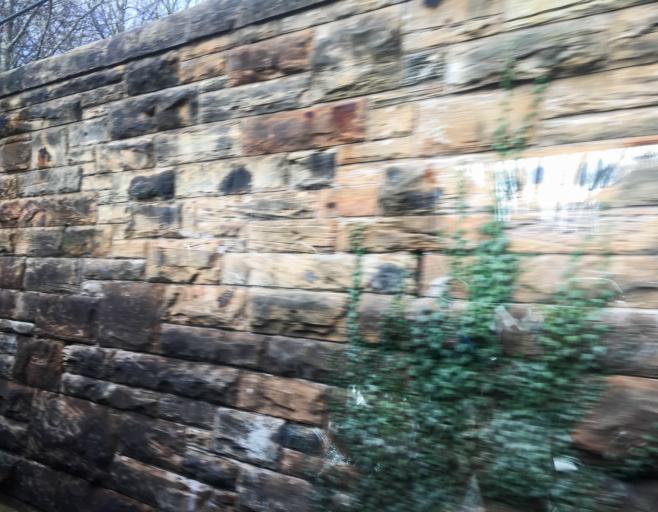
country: GB
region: Scotland
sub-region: North Lanarkshire
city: Wishaw
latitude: 55.7774
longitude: -3.9390
